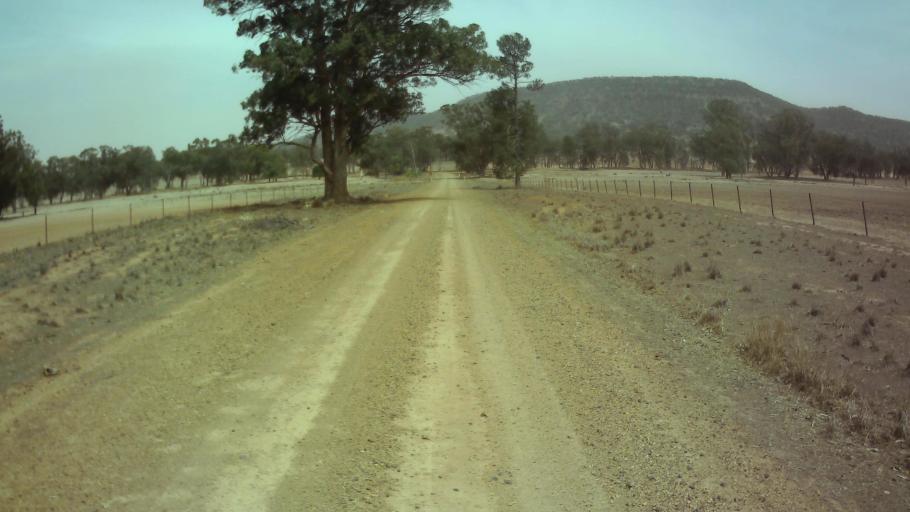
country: AU
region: New South Wales
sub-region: Weddin
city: Grenfell
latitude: -33.7439
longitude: 147.9647
